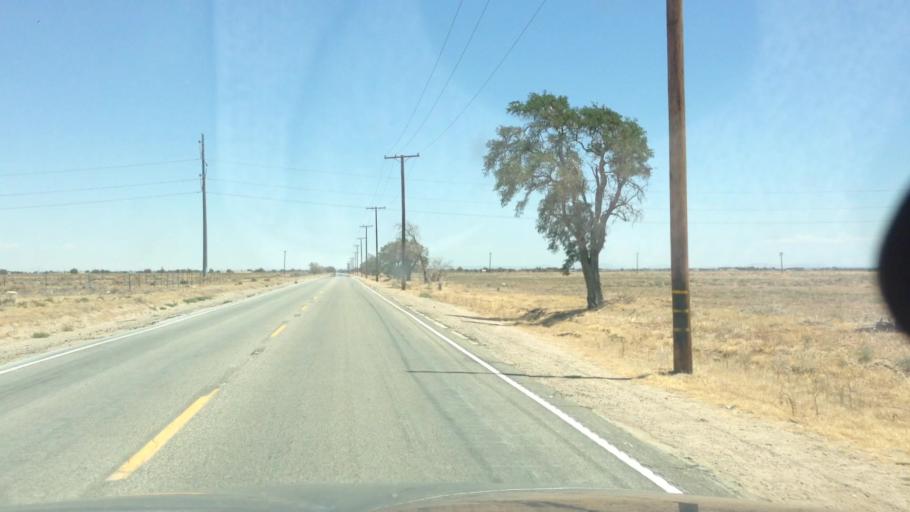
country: US
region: California
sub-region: Los Angeles County
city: Leona Valley
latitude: 34.7761
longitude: -118.3214
